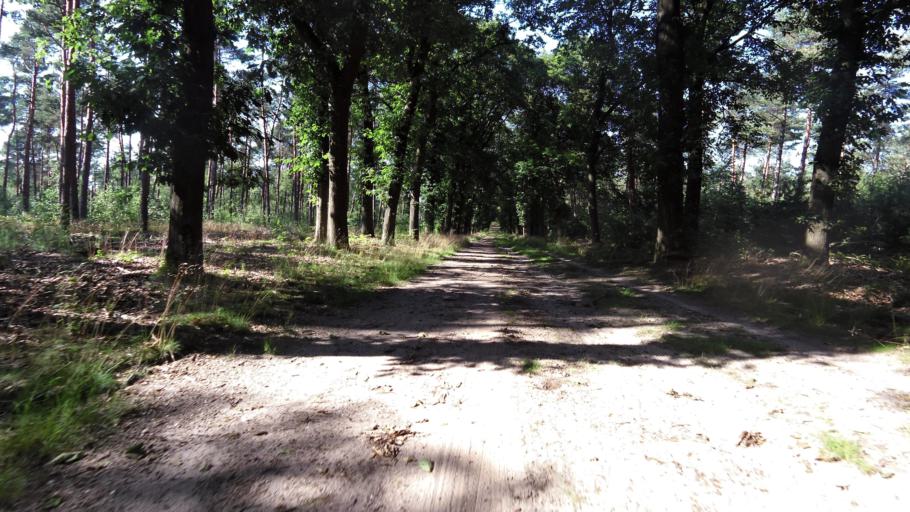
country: NL
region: Gelderland
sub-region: Gemeente Arnhem
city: Hoogkamp
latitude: 52.0171
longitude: 5.8847
